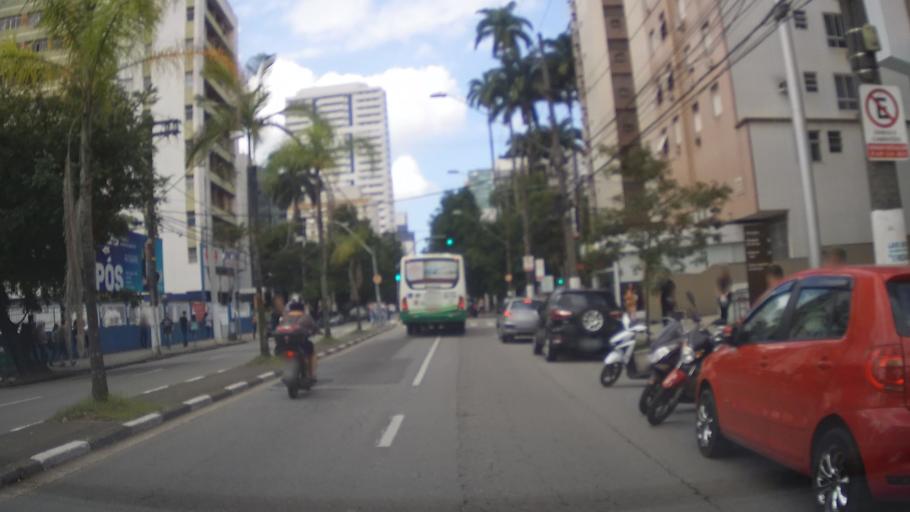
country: BR
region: Sao Paulo
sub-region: Santos
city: Santos
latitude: -23.9625
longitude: -46.3234
